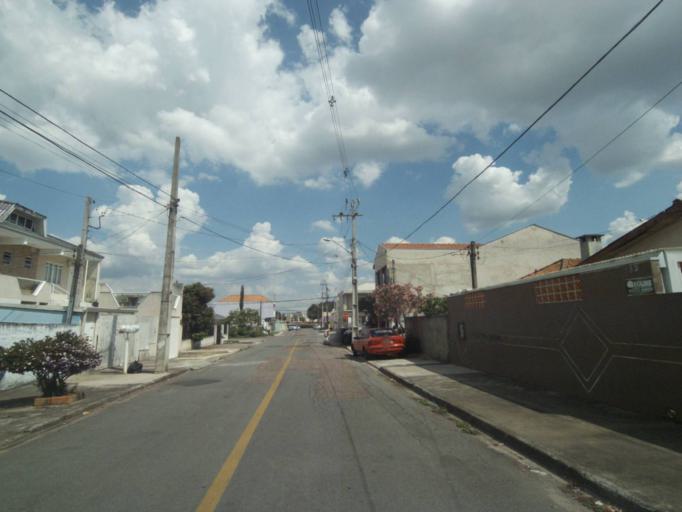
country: BR
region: Parana
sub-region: Sao Jose Dos Pinhais
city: Sao Jose dos Pinhais
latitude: -25.5330
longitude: -49.2570
